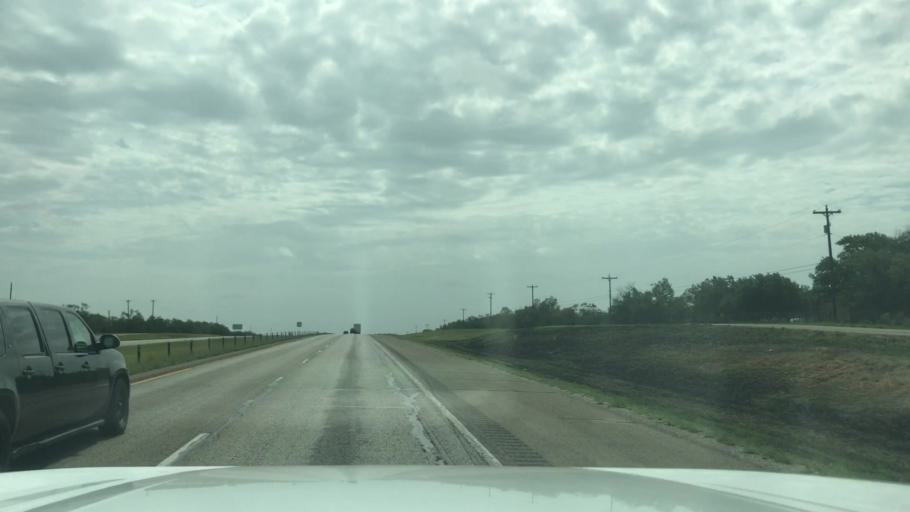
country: US
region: Texas
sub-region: Callahan County
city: Clyde
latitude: 32.4215
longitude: -99.5450
